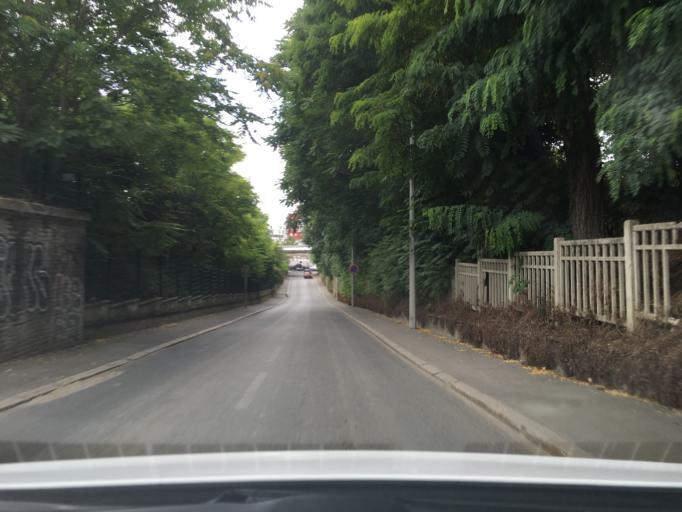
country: FR
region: Ile-de-France
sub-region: Departement des Hauts-de-Seine
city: Nanterre
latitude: 48.9026
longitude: 2.2215
